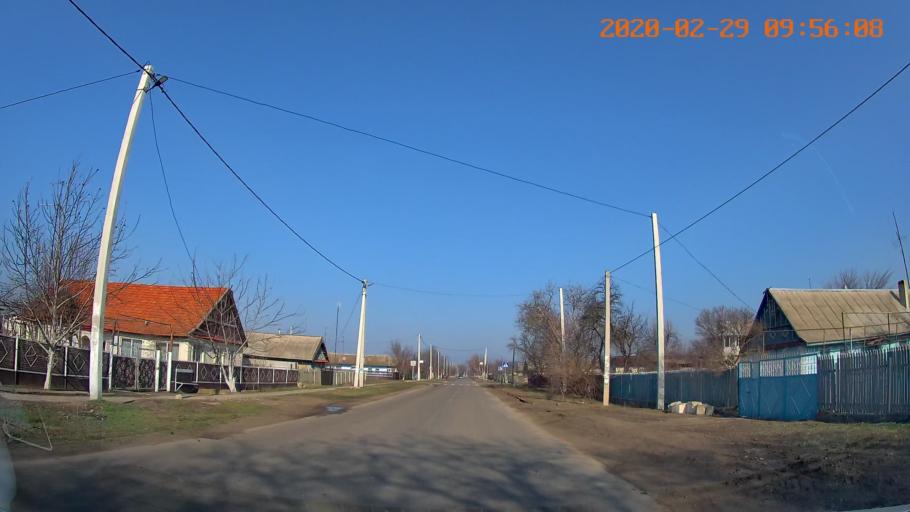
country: MD
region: Telenesti
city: Slobozia
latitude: 46.7398
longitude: 29.7064
